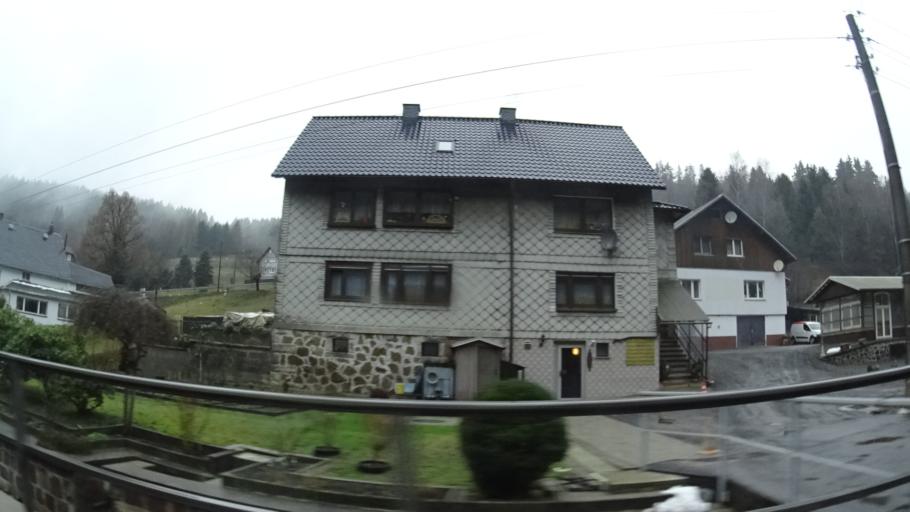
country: DE
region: Thuringia
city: Eisfeld
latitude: 50.4909
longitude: 10.9113
